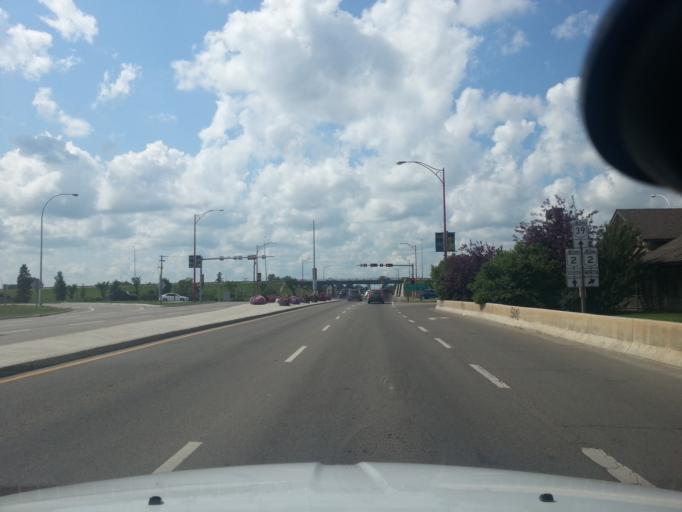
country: CA
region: Alberta
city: Leduc
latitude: 53.2648
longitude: -113.5604
